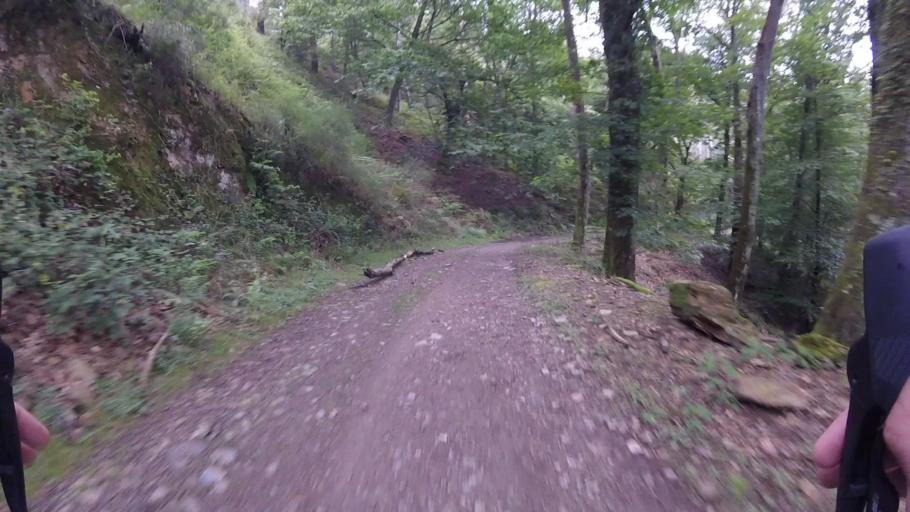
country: ES
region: Navarre
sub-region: Provincia de Navarra
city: Arano
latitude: 43.2529
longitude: -1.8694
